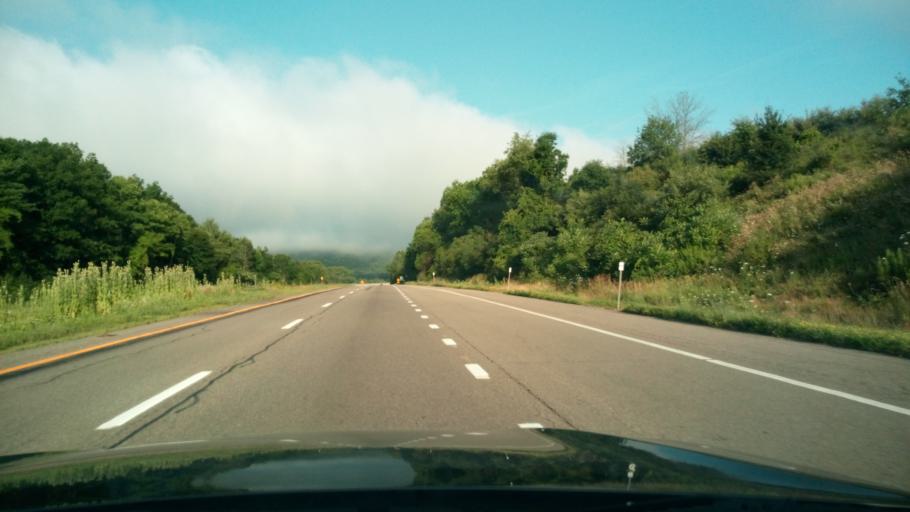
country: US
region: New York
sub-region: Steuben County
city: Gang Mills
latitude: 42.1867
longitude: -77.1474
